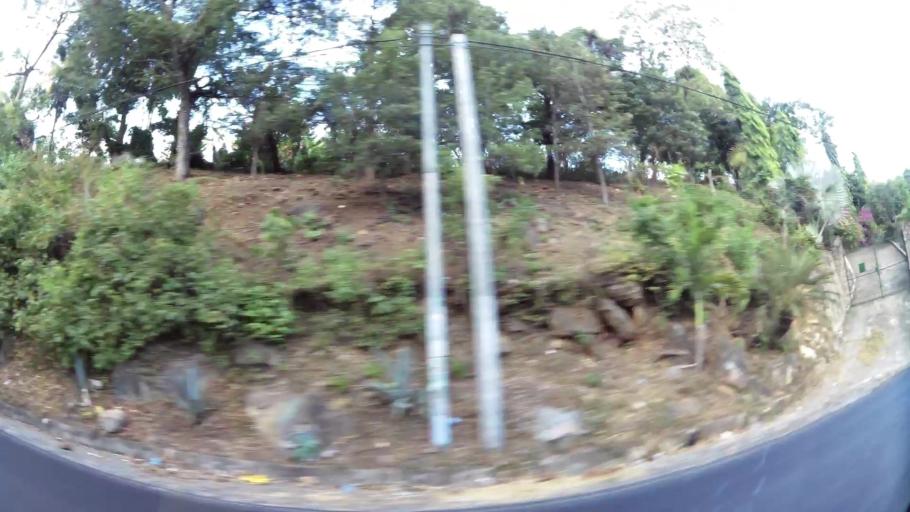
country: SV
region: San Vicente
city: Apastepeque
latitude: 13.6504
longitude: -88.7852
